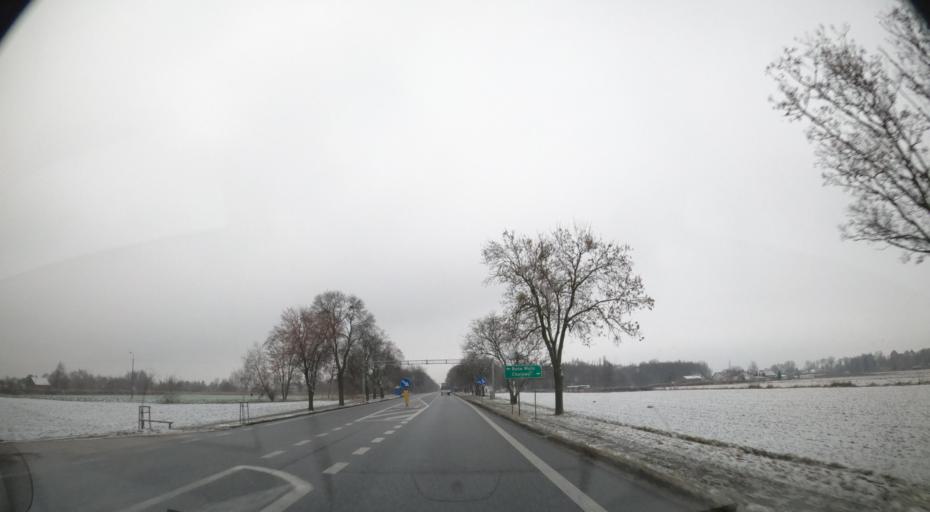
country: PL
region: Masovian Voivodeship
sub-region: Powiat warszawski zachodni
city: Bieniewice
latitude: 52.2027
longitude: 20.5309
